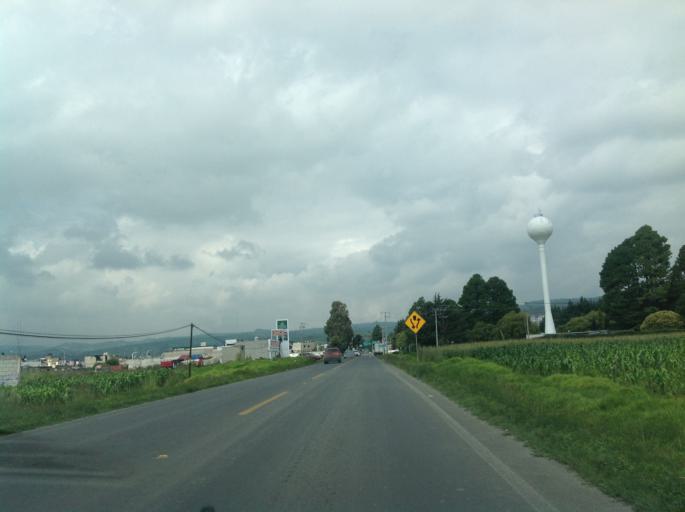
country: MX
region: Morelos
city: Tenango de Arista
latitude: 19.1071
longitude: -99.5766
